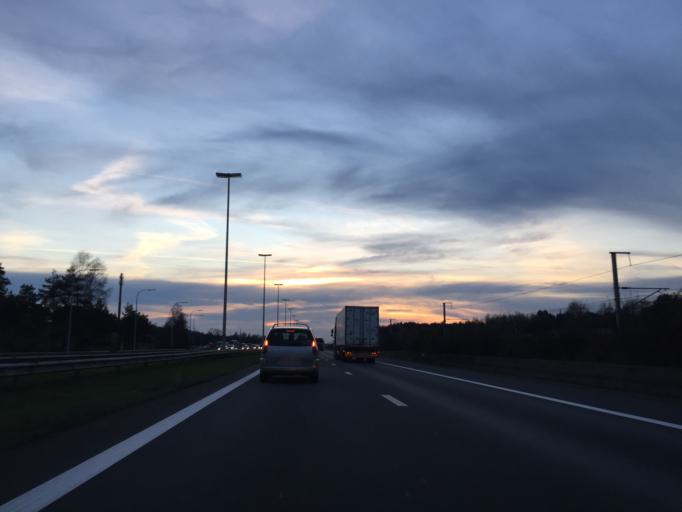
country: BE
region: Flanders
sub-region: Provincie Antwerpen
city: Brecht
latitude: 51.3252
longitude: 4.5908
